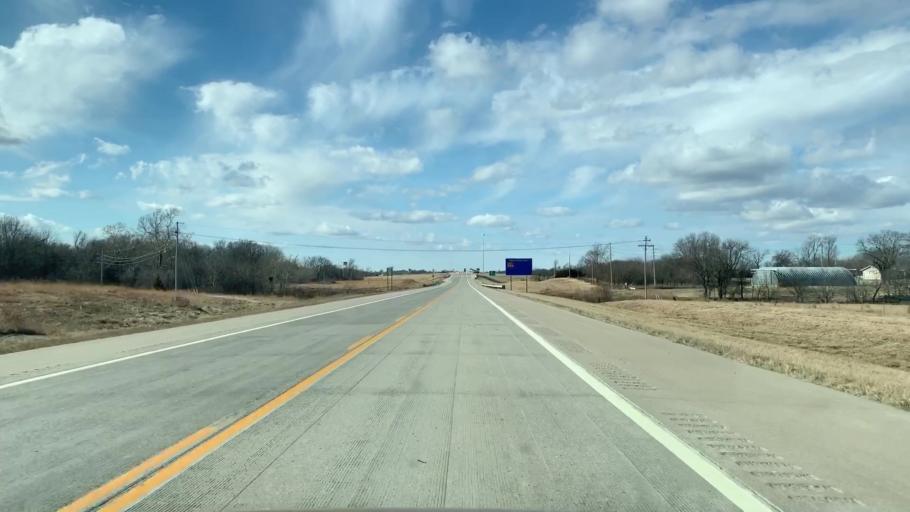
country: US
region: Kansas
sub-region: Labette County
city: Parsons
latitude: 37.3648
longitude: -95.2472
